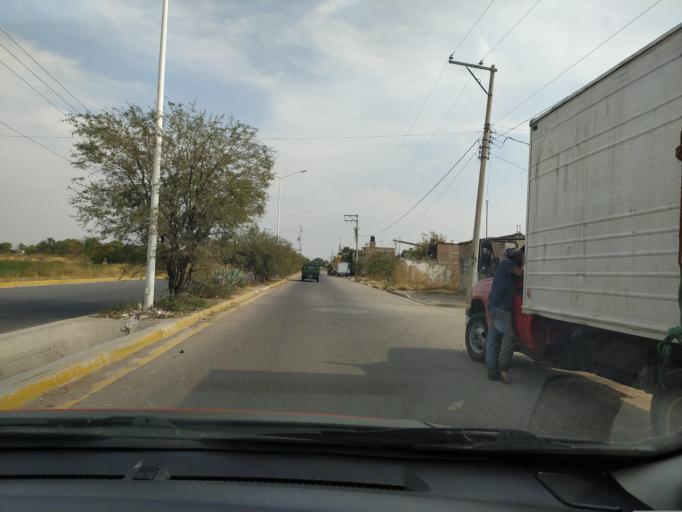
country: MX
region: Guanajuato
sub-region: San Francisco del Rincon
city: Fraccionamiento la Mezquitera
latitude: 21.0175
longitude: -101.8332
